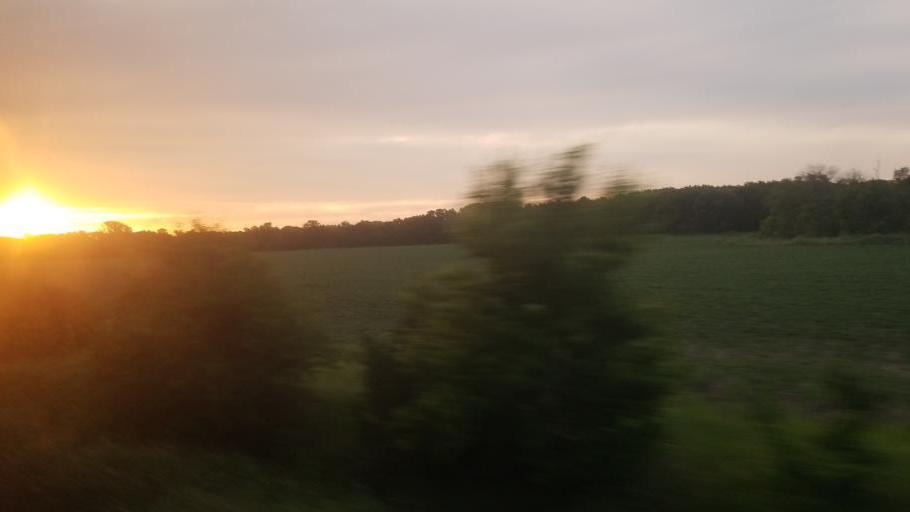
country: US
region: Kansas
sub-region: Marion County
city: Peabody
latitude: 38.1540
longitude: -97.1208
